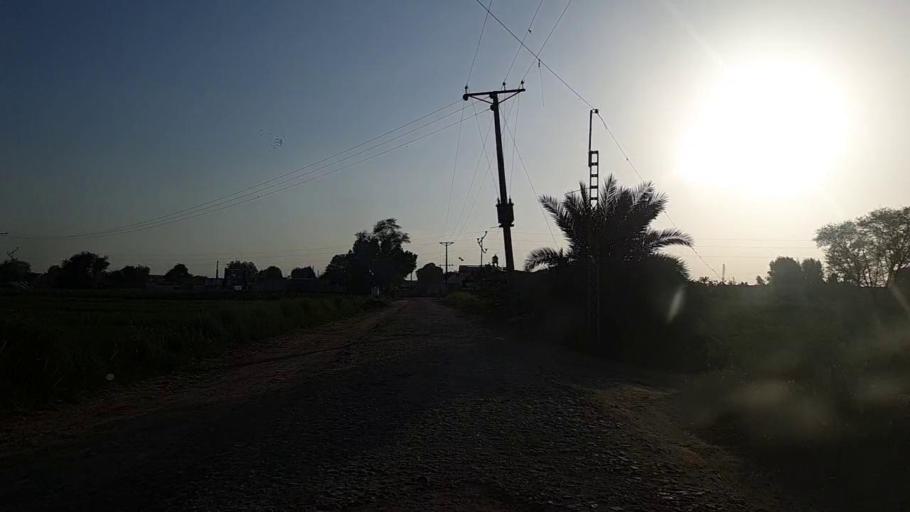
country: PK
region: Sindh
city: Hingorja
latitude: 27.0573
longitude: 68.4047
